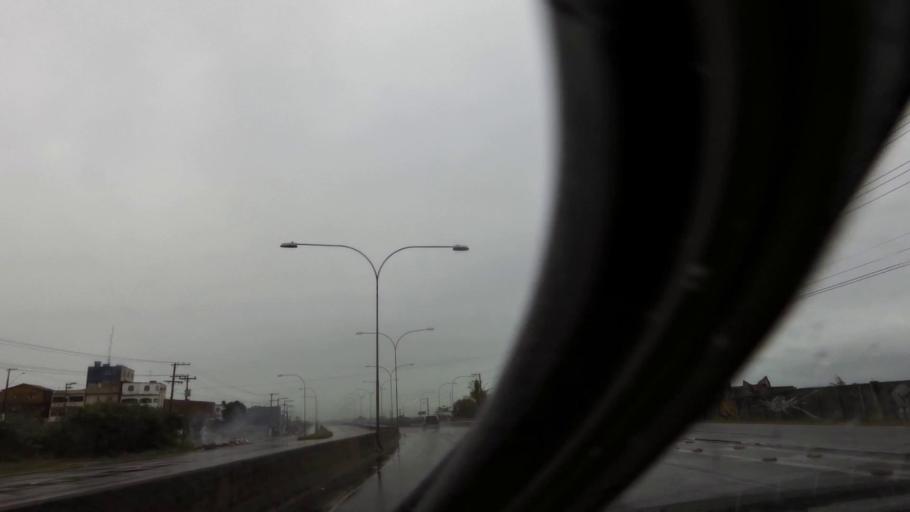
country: BR
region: Espirito Santo
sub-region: Vila Velha
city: Vila Velha
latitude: -20.4509
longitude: -40.3349
